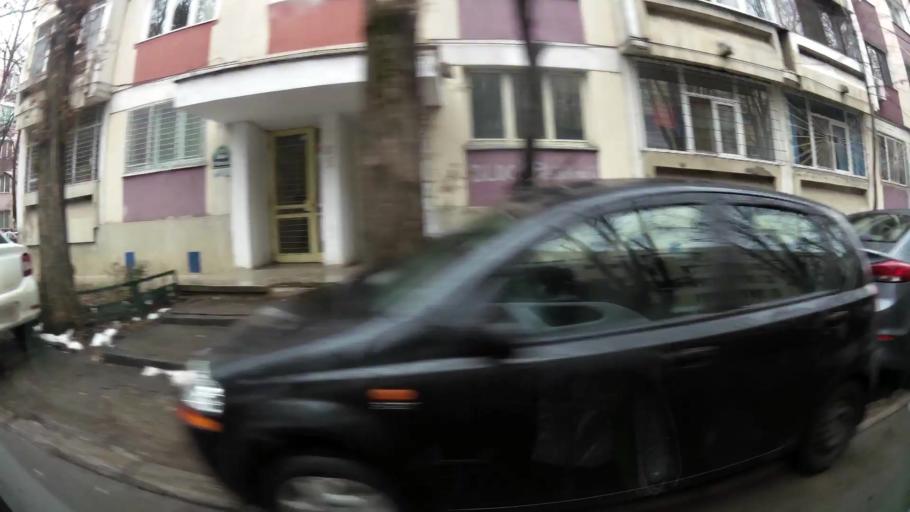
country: RO
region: Ilfov
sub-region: Comuna Chiajna
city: Rosu
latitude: 44.4360
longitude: 26.0422
